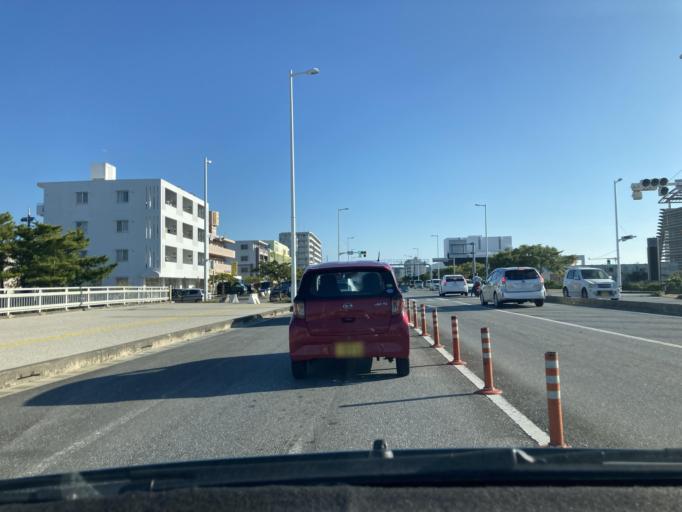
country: JP
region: Okinawa
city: Itoman
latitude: 26.1252
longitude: 127.6667
